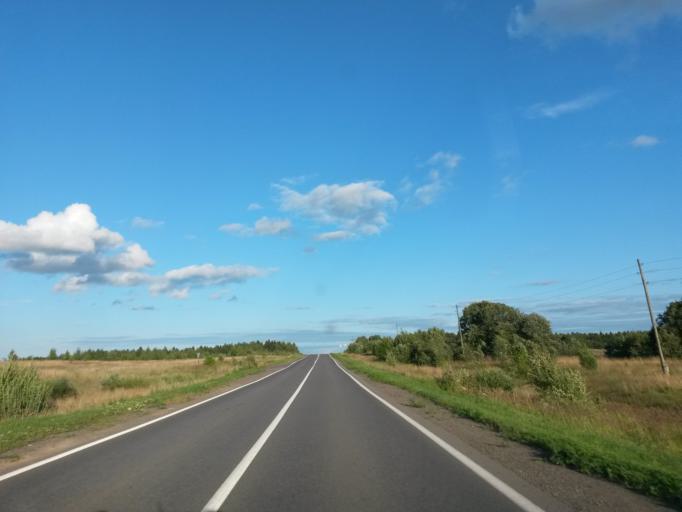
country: RU
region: Jaroslavl
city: Konstantinovskiy
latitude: 57.8194
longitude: 39.7020
